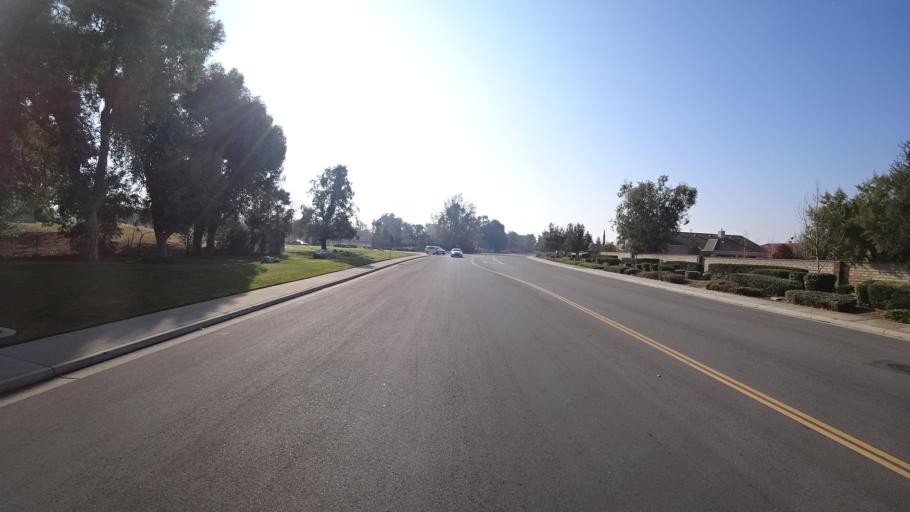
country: US
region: California
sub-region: Kern County
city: Lamont
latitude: 35.4068
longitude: -118.8433
